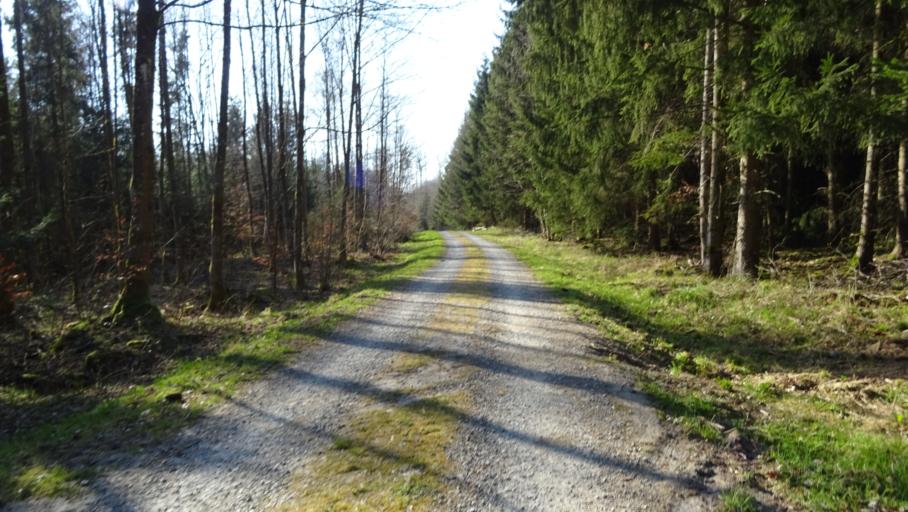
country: DE
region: Baden-Wuerttemberg
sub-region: Regierungsbezirk Stuttgart
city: Roigheim
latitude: 49.3975
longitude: 9.3064
